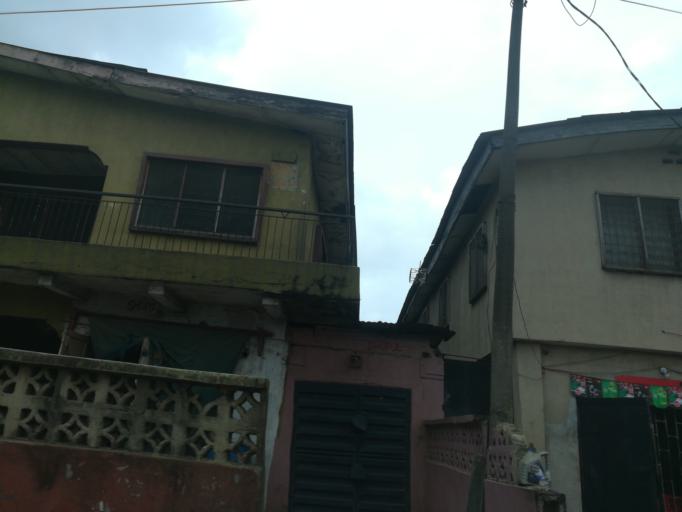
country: NG
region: Lagos
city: Oshodi
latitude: 6.5539
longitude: 3.3329
